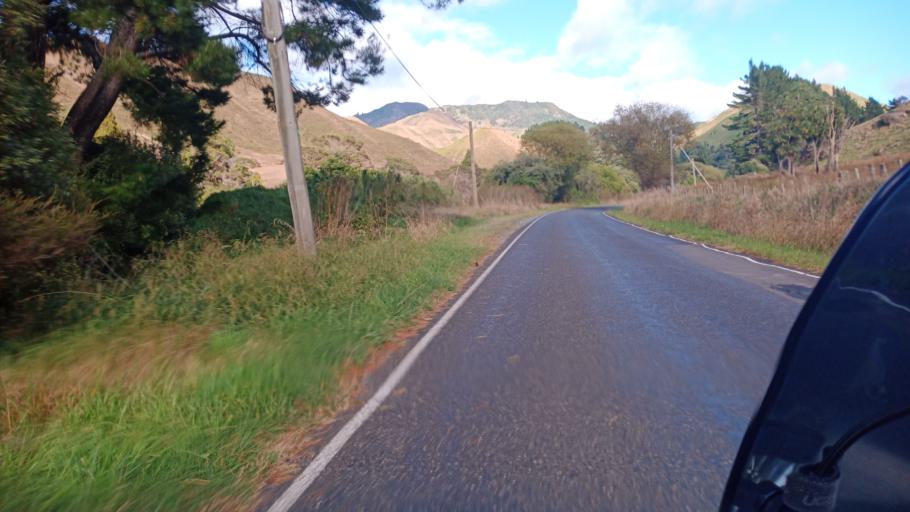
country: NZ
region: Gisborne
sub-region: Gisborne District
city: Gisborne
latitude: -38.5395
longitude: 177.5692
